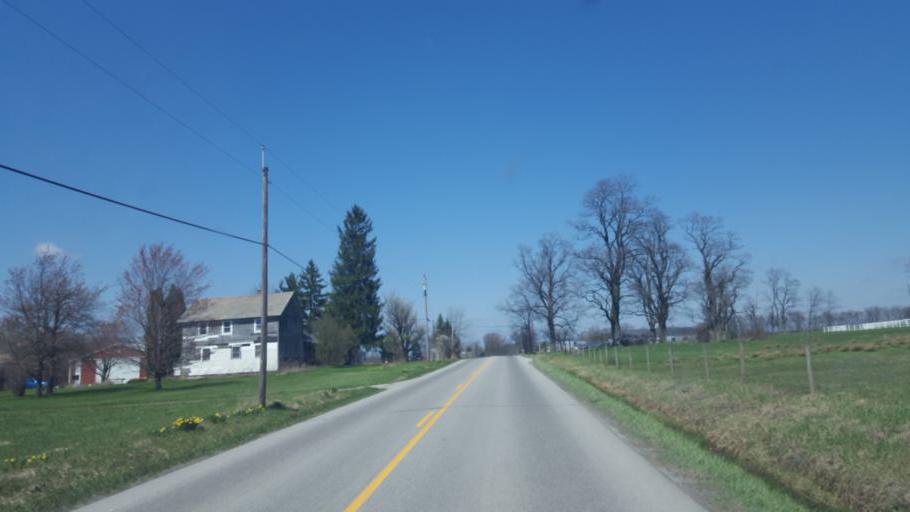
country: US
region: Ohio
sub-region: Geauga County
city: Middlefield
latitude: 41.3987
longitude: -81.1083
